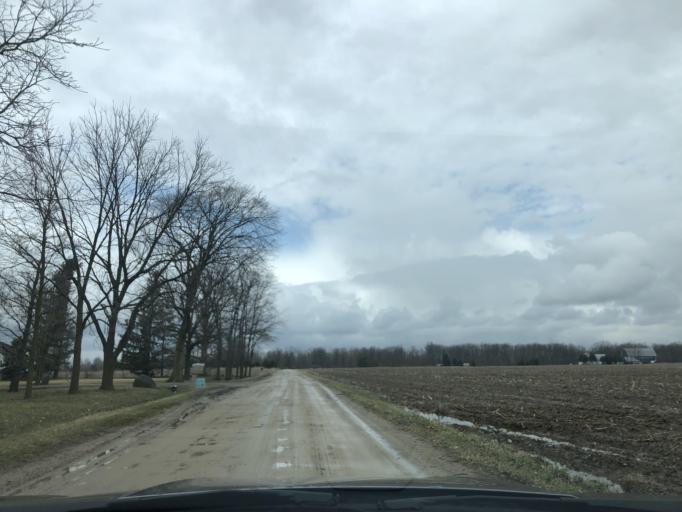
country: US
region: Michigan
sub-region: Clinton County
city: Saint Johns
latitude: 43.0419
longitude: -84.6411
